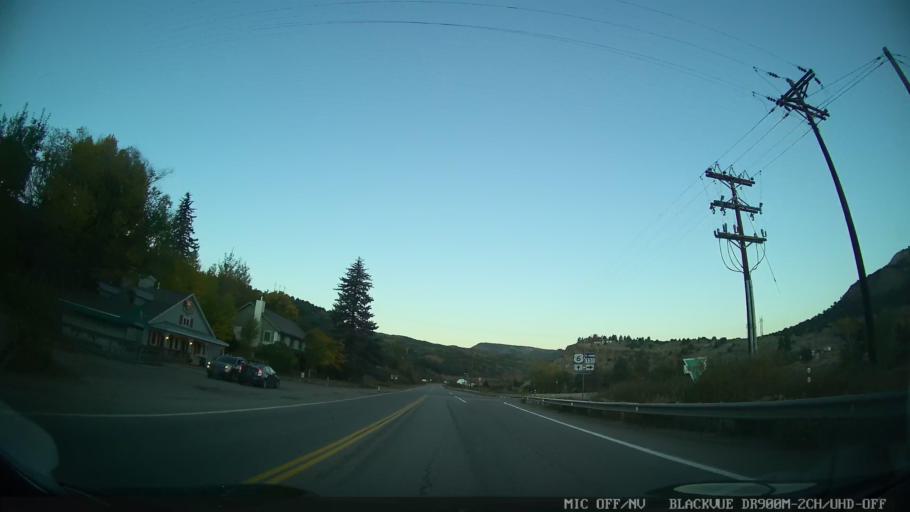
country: US
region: Colorado
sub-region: Eagle County
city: Edwards
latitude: 39.7011
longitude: -106.6769
